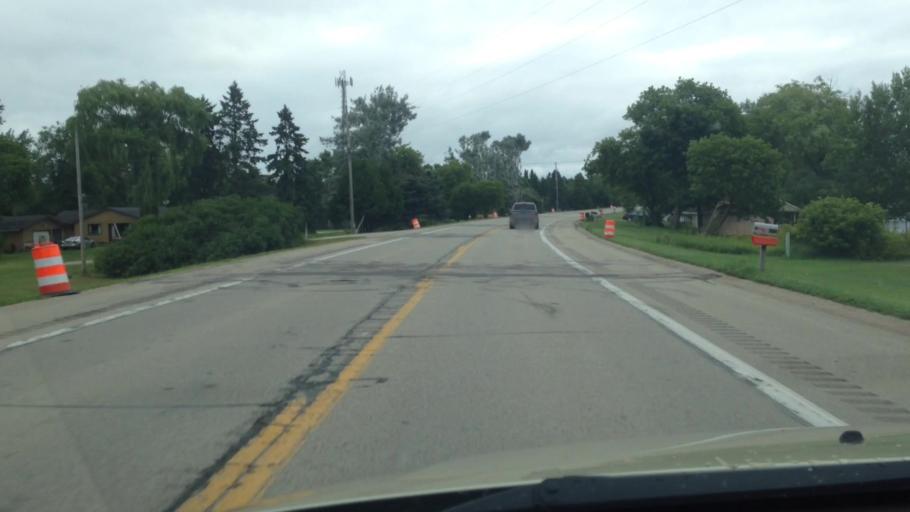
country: US
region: Michigan
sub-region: Delta County
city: Escanaba
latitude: 45.6387
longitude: -87.1978
